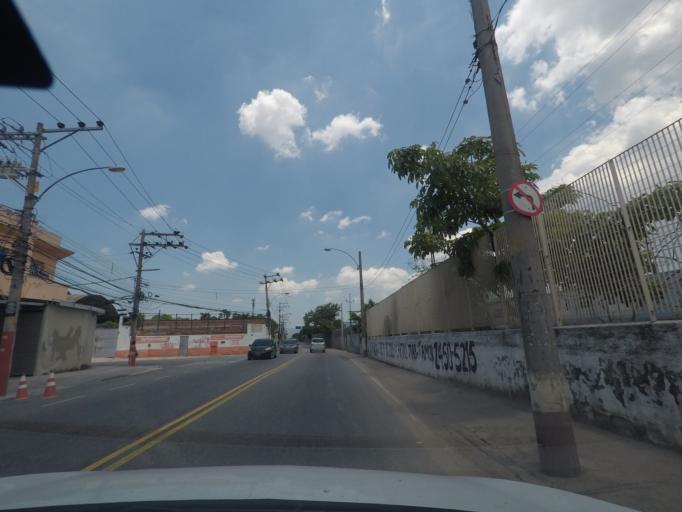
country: BR
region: Rio de Janeiro
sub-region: Sao Joao De Meriti
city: Sao Joao de Meriti
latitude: -22.8696
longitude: -43.3489
